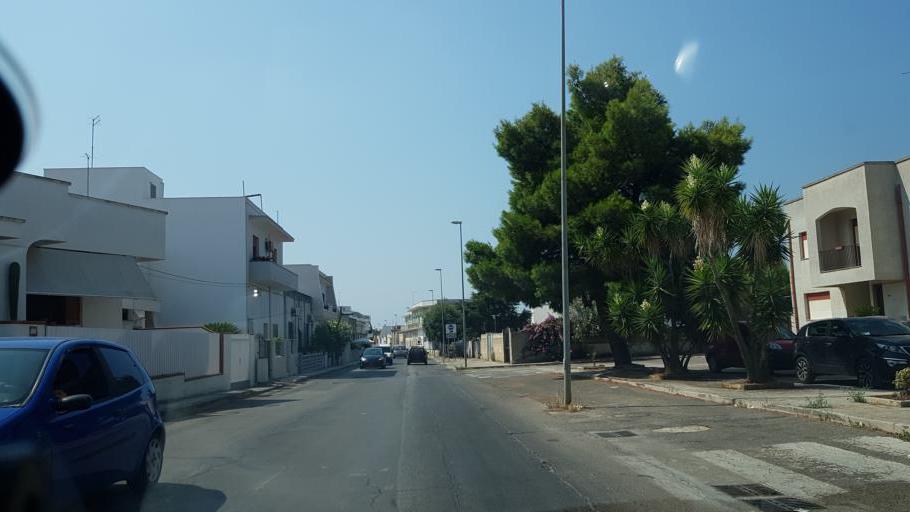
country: IT
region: Apulia
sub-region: Provincia di Taranto
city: Maruggio
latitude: 40.3271
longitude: 17.5734
